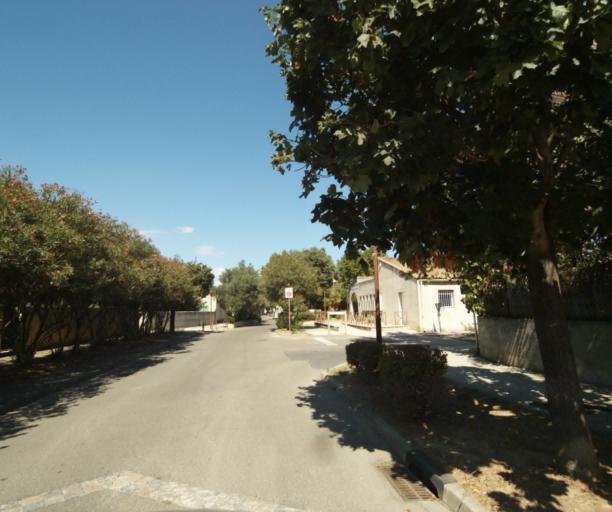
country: FR
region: Languedoc-Roussillon
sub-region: Departement du Gard
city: Rodilhan
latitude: 43.8255
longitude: 4.4309
